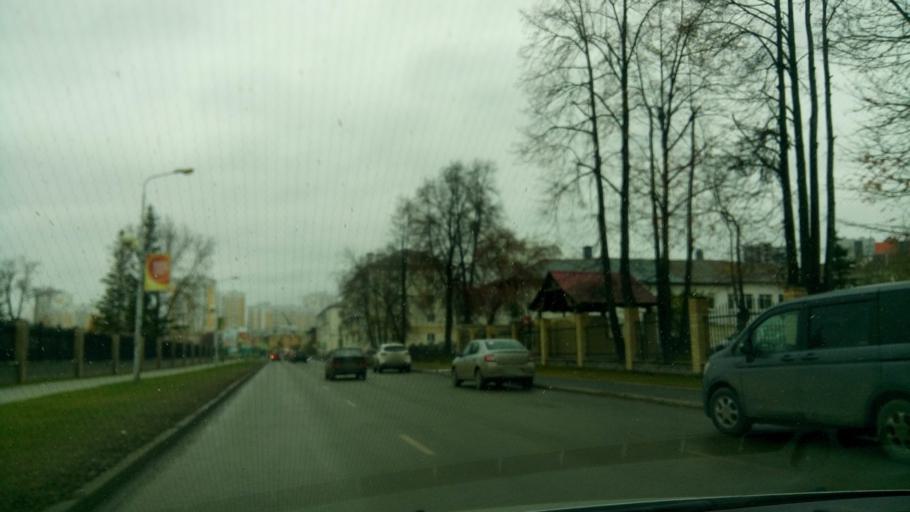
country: RU
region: Sverdlovsk
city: Verkhnyaya Pyshma
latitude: 56.9677
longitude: 60.5799
